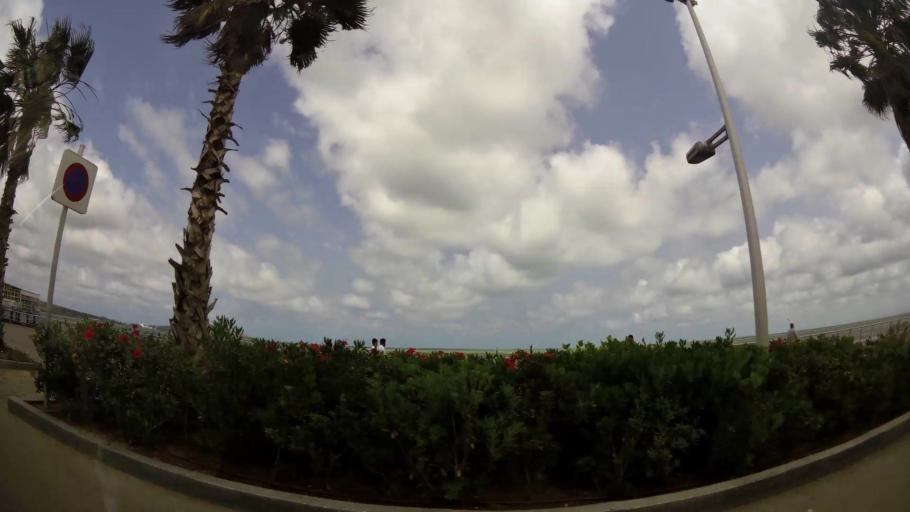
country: MA
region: Oriental
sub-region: Nador
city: Nador
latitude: 35.1807
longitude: -2.9225
